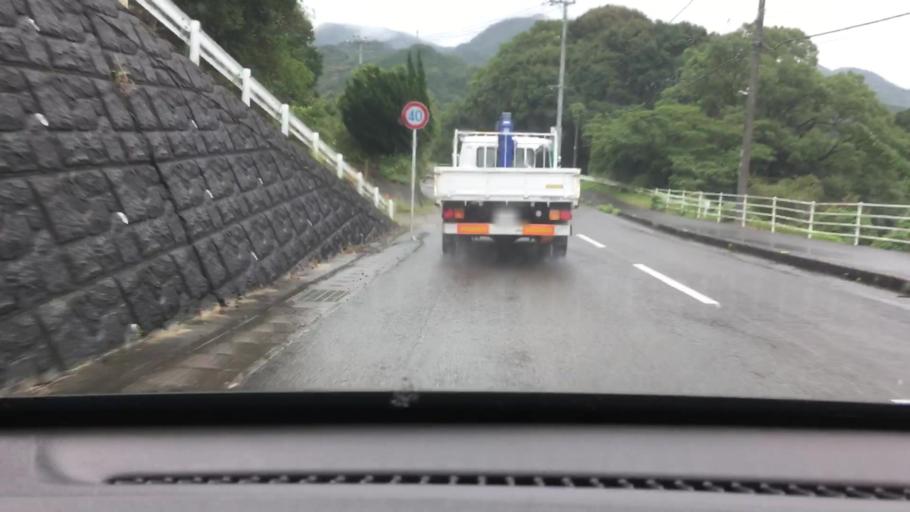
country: JP
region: Nagasaki
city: Togitsu
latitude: 32.8562
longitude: 129.7803
